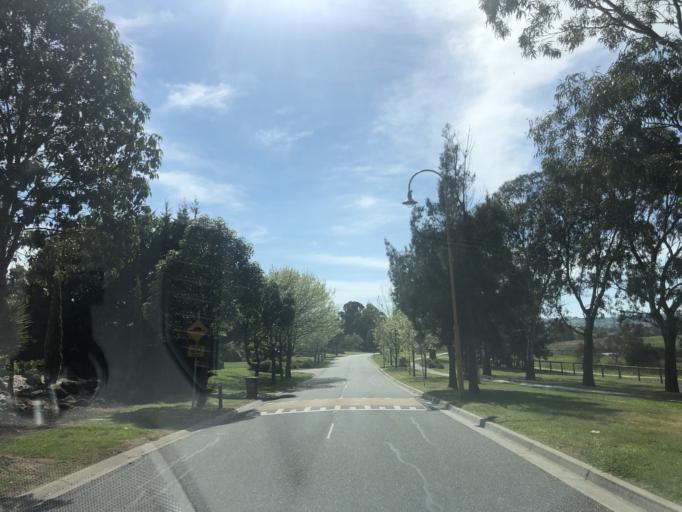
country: AU
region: Victoria
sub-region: Casey
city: Hallam
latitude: -37.9965
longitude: 145.2880
